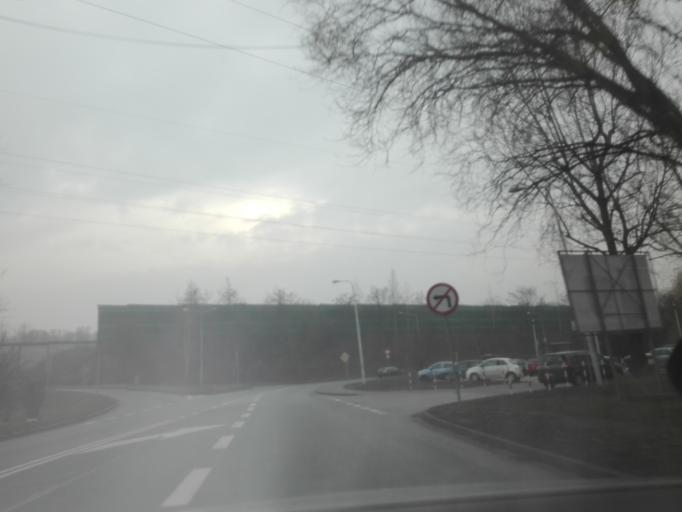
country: PL
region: Silesian Voivodeship
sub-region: Chorzow
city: Chorzow
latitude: 50.2563
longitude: 18.9716
